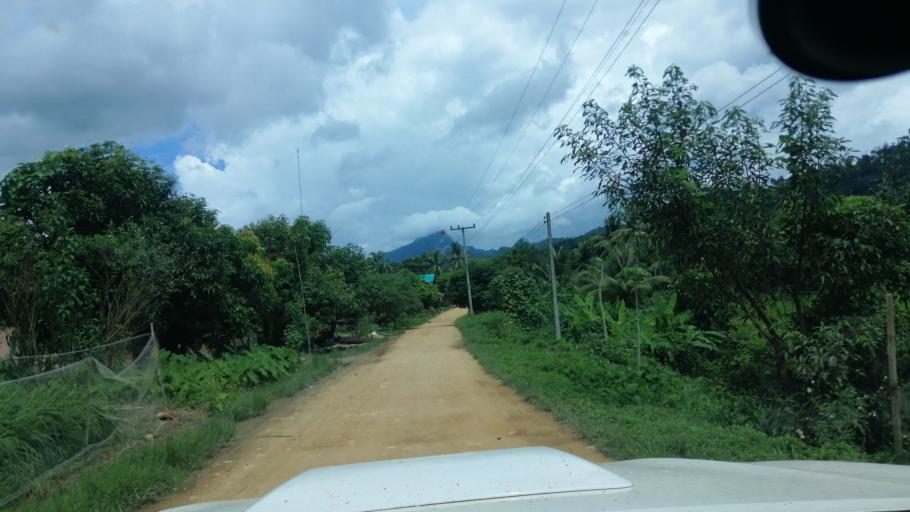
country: TH
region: Phayao
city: Phu Sang
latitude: 19.7097
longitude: 100.4893
